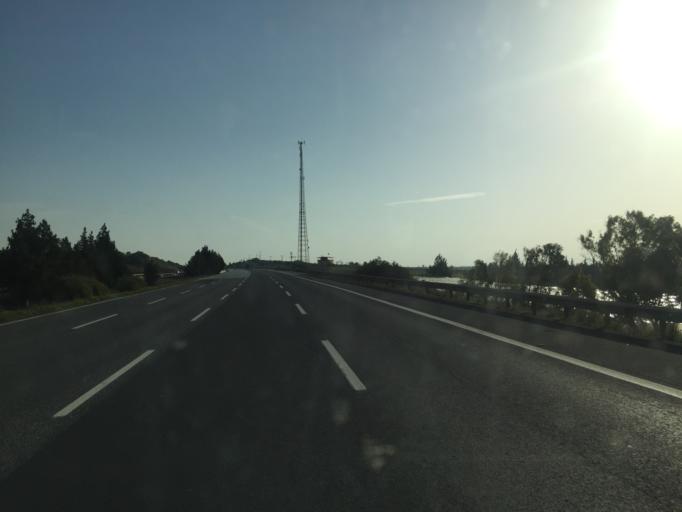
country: TR
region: Mersin
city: Yenice
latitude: 37.0225
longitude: 35.0826
